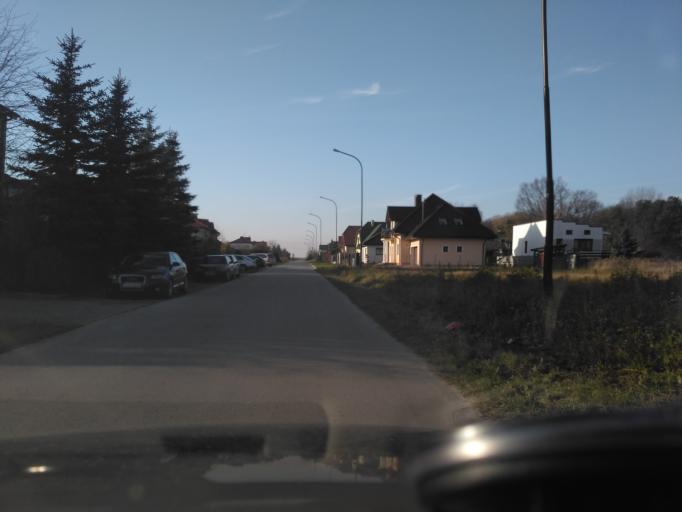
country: PL
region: Lublin Voivodeship
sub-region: Powiat lubelski
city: Lublin
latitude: 51.1740
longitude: 22.5843
